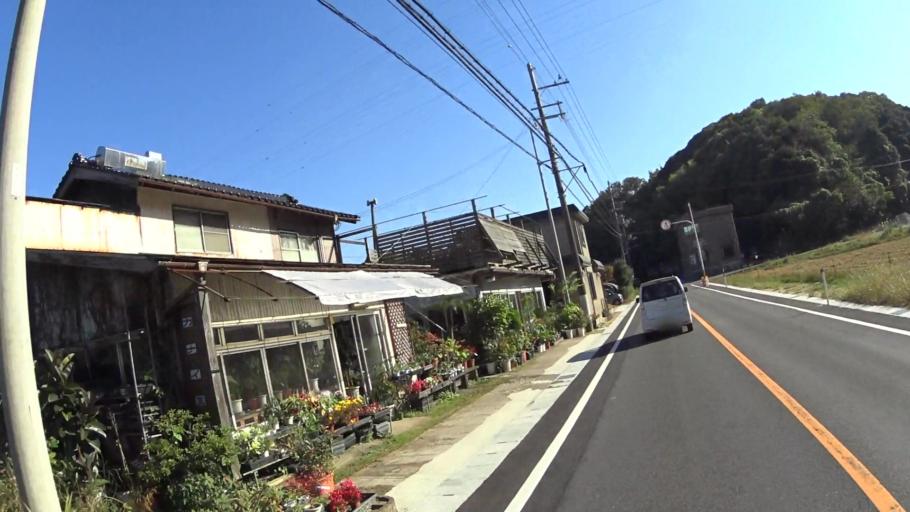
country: JP
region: Kyoto
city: Miyazu
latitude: 35.6657
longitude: 135.0282
